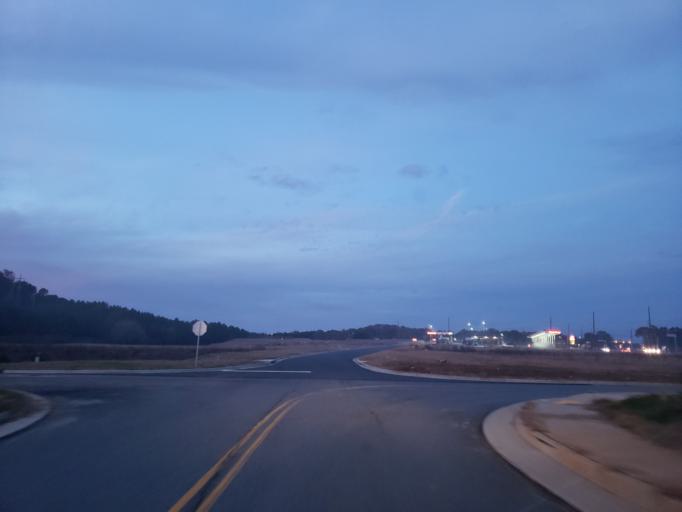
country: US
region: Georgia
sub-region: Bartow County
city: Cartersville
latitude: 34.2051
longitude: -84.8009
